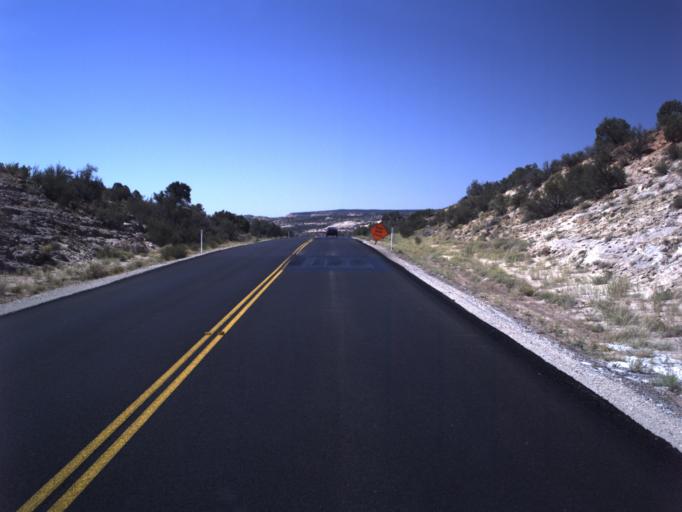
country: US
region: Utah
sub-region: San Juan County
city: Blanding
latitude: 37.5519
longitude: -109.6087
